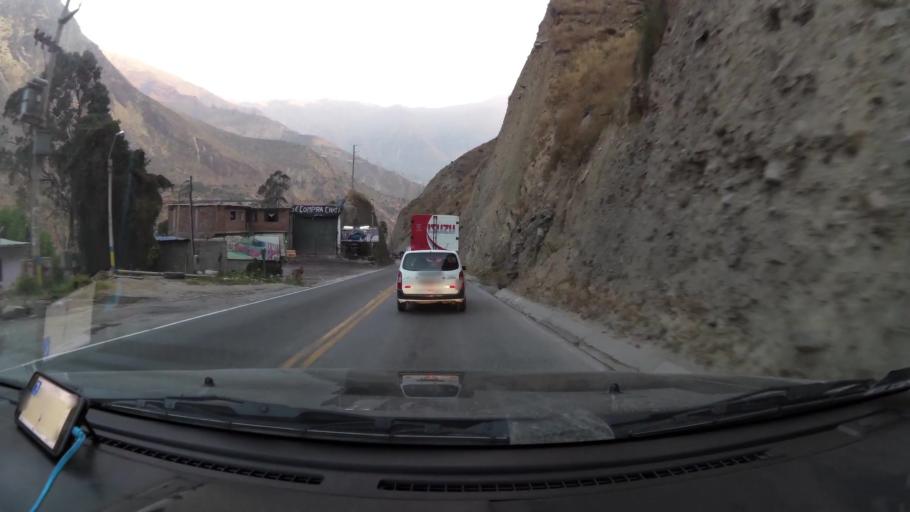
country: PE
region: Lima
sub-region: Provincia de Huarochiri
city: Surco
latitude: -11.8666
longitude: -76.4254
